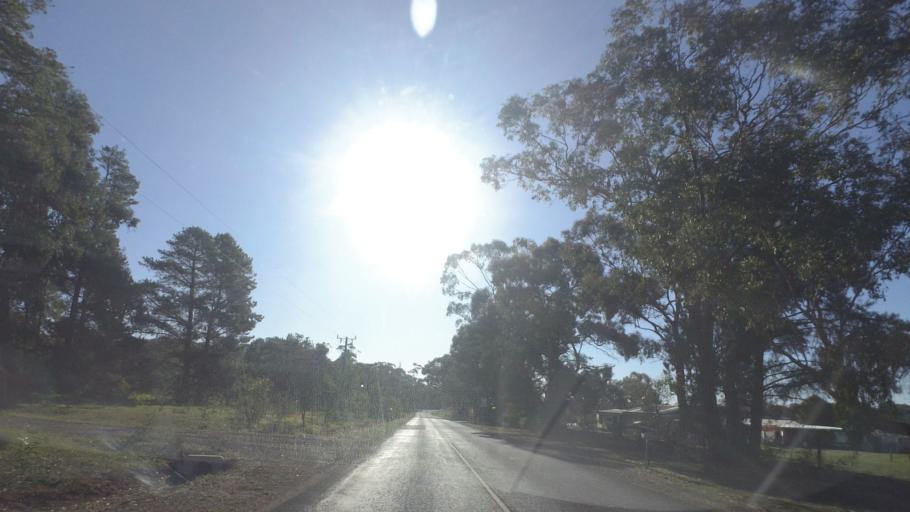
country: AU
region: Victoria
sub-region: Greater Bendigo
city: Kangaroo Flat
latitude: -36.8550
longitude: 144.2810
